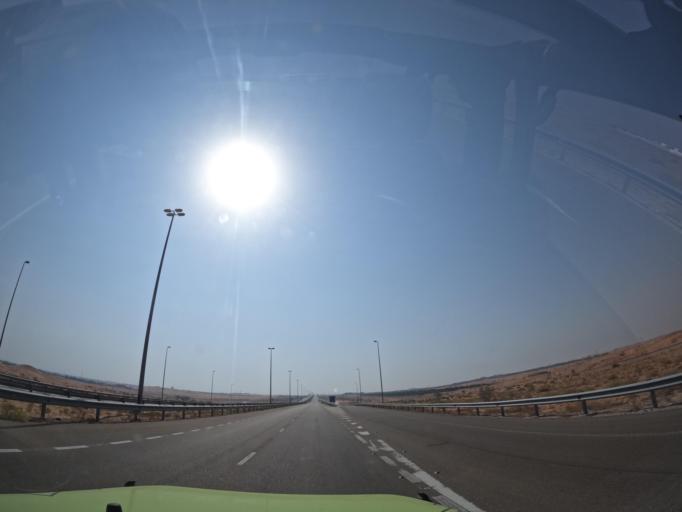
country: OM
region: Al Buraimi
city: Al Buraymi
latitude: 24.4105
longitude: 55.7020
